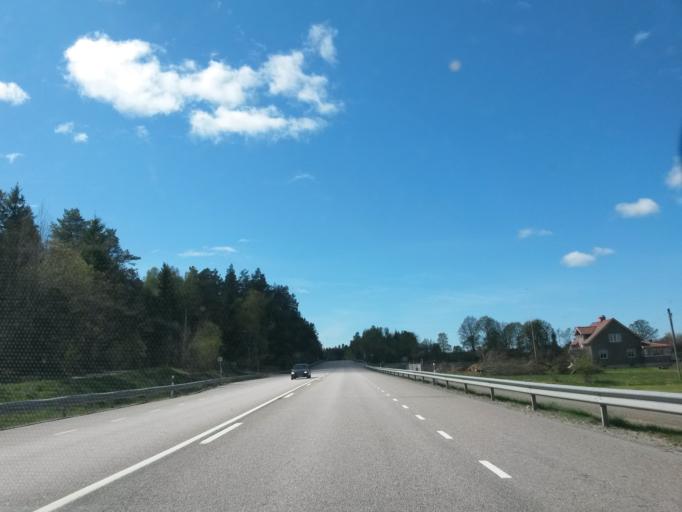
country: SE
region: Vaestra Goetaland
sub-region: Vargarda Kommun
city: Jonstorp
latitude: 57.9936
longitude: 12.7081
